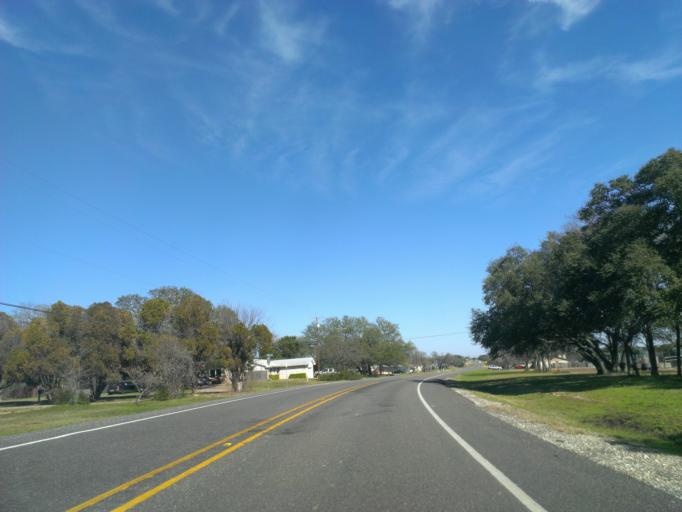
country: US
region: Texas
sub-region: Bell County
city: Belton
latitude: 31.0380
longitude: -97.5258
